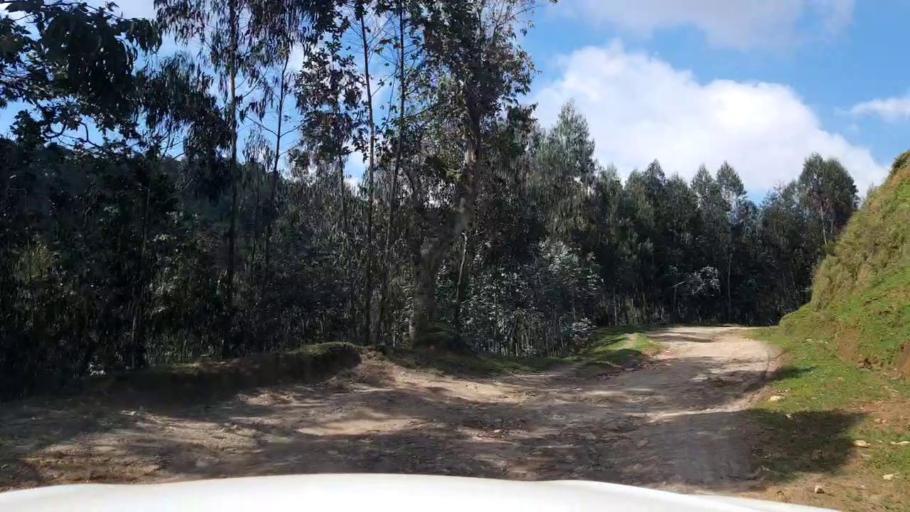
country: RW
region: Western Province
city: Kibuye
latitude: -1.8829
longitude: 29.4680
